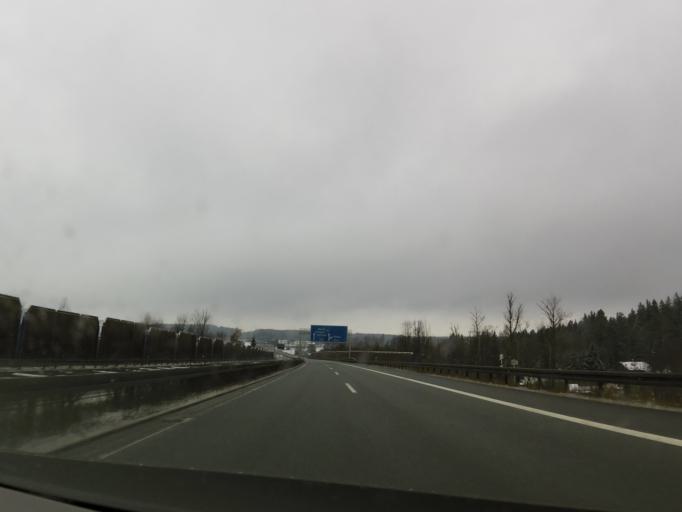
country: DE
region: Bavaria
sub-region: Upper Franconia
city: Rehau
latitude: 50.2534
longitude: 12.0550
